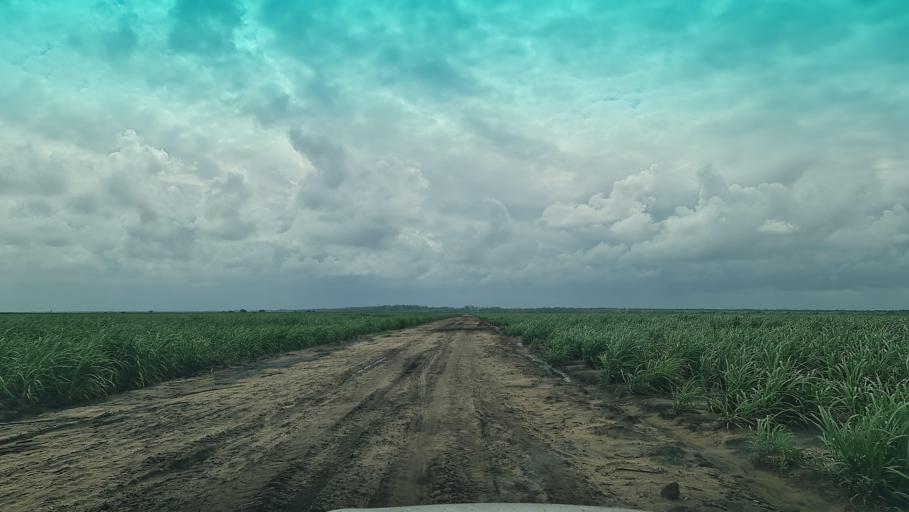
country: MZ
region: Maputo
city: Manhica
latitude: -25.4530
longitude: 32.8279
